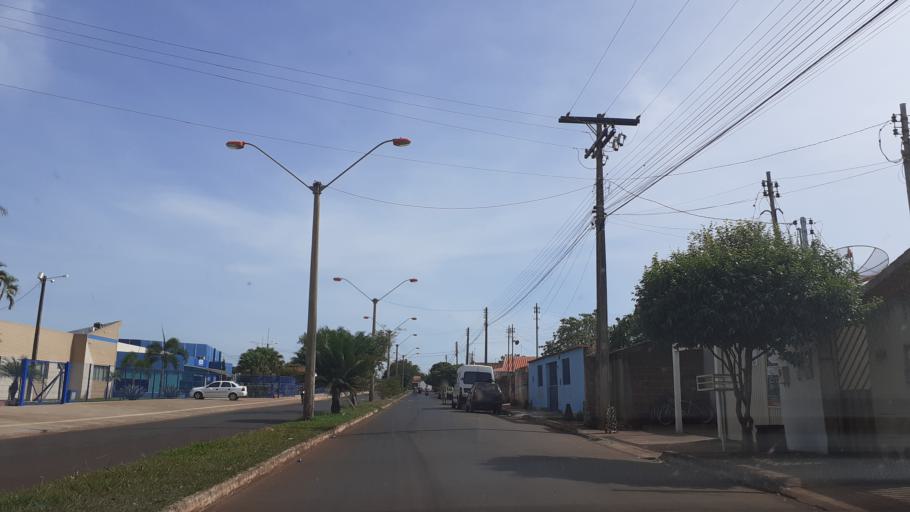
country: BR
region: Goias
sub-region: Itumbiara
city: Itumbiara
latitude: -18.4181
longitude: -49.2330
